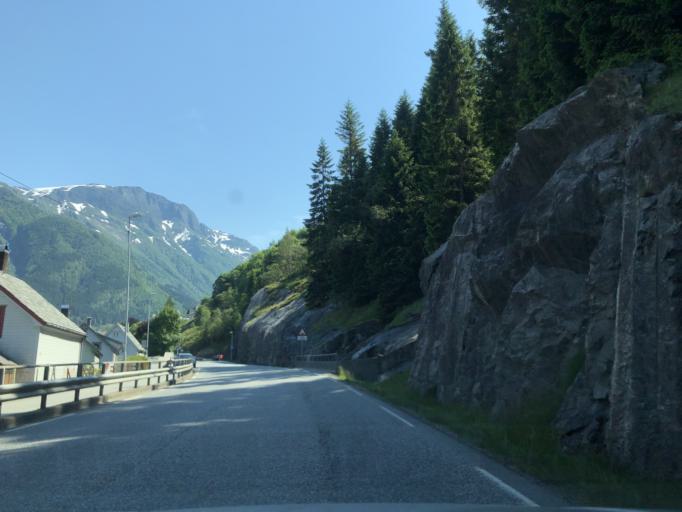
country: NO
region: Hordaland
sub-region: Odda
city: Odda
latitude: 60.0773
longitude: 6.5310
